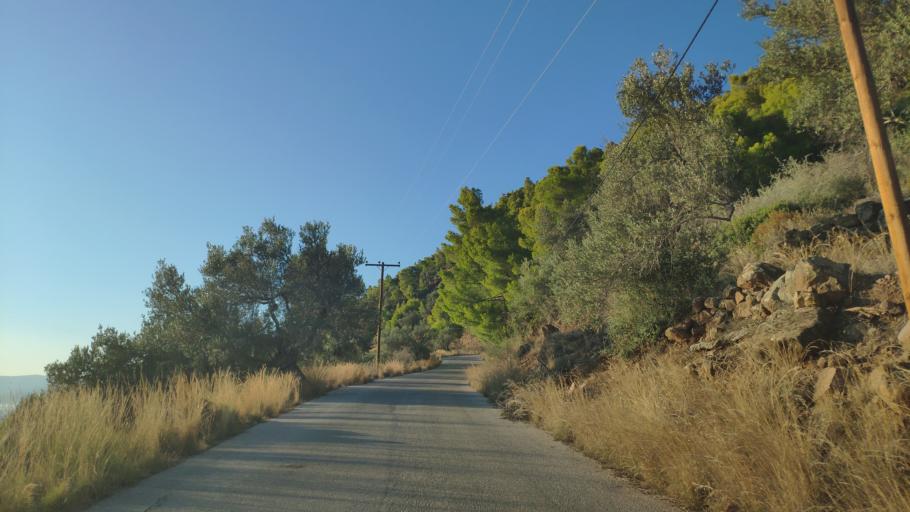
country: GR
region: Attica
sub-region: Nomos Piraios
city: Megalochori
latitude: 37.6009
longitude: 23.3351
